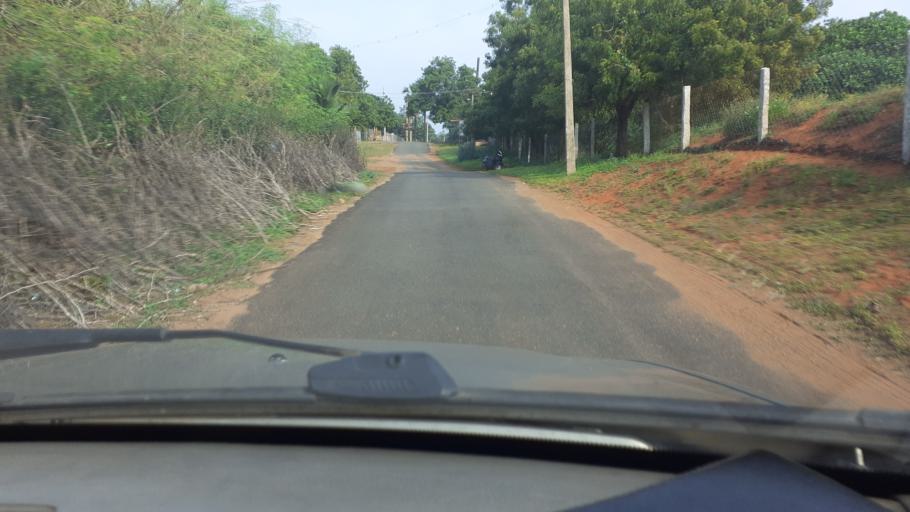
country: IN
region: Tamil Nadu
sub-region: Tirunelveli Kattabo
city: Tisaiyanvilai
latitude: 8.3360
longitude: 77.9526
